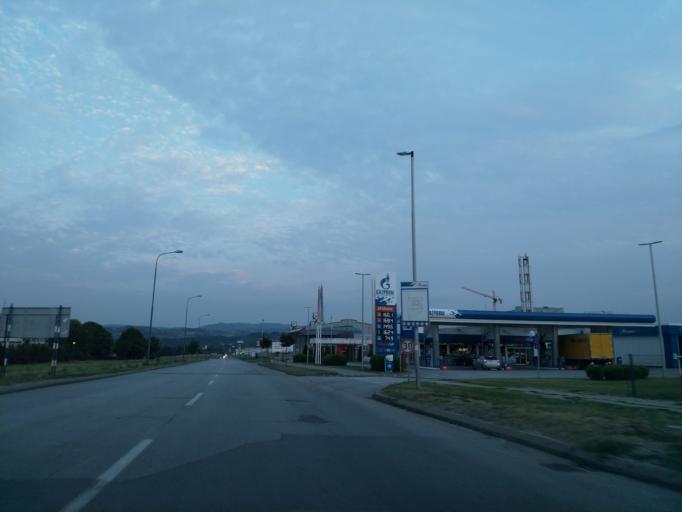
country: RS
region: Central Serbia
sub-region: Sumadijski Okrug
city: Kragujevac
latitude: 44.0289
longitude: 20.9179
